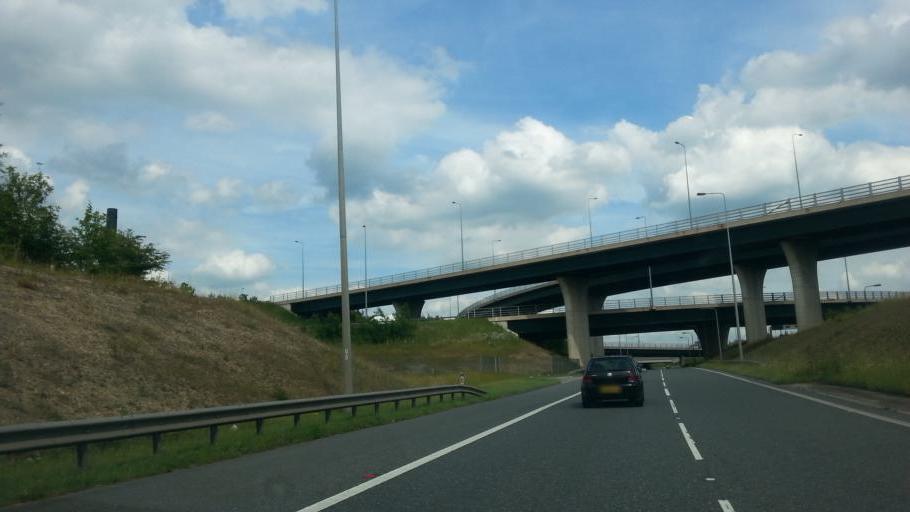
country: GB
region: England
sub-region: City and Borough of Wakefield
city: Ferrybridge
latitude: 53.7119
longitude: -1.2929
